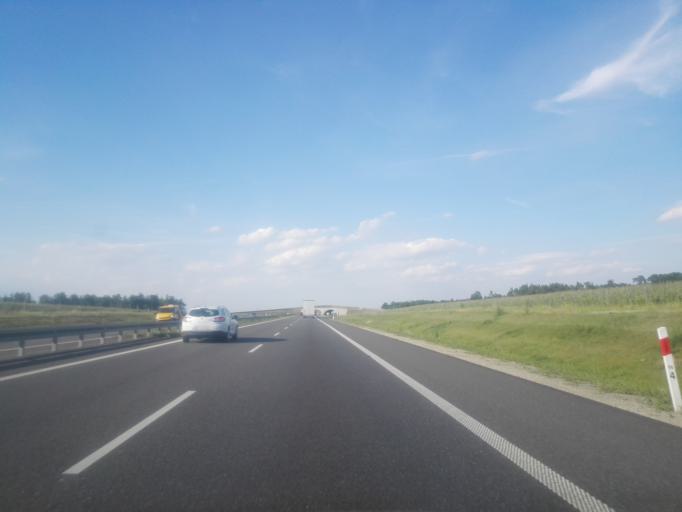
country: PL
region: Lower Silesian Voivodeship
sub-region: Powiat olesnicki
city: Twardogora
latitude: 51.2692
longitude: 17.5534
